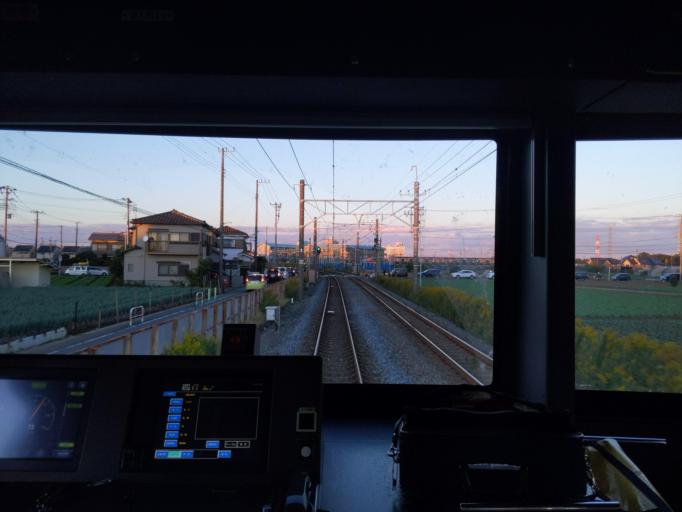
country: JP
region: Chiba
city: Funabashi
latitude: 35.7308
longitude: 139.9901
